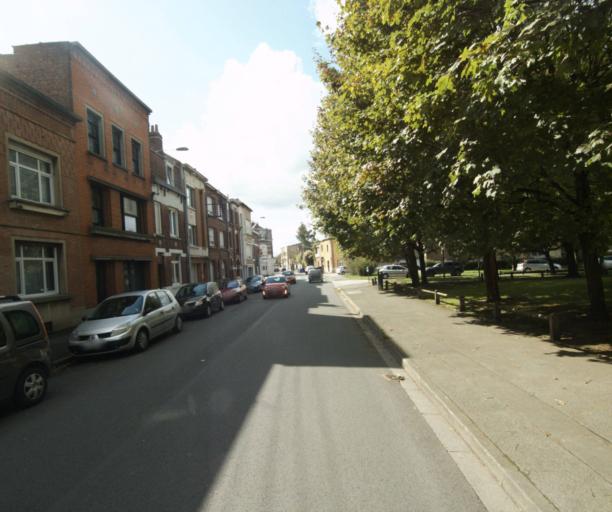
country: FR
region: Nord-Pas-de-Calais
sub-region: Departement du Nord
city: Loos
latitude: 50.6154
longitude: 3.0271
